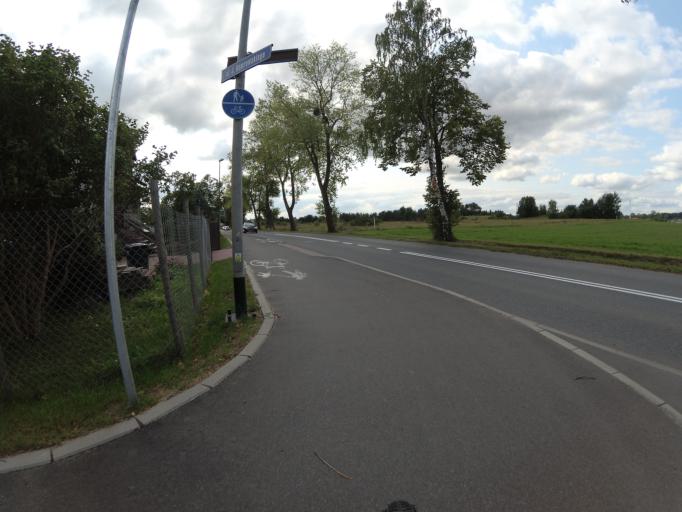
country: PL
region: Pomeranian Voivodeship
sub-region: Powiat wejherowski
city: Bojano
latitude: 54.4968
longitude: 18.4307
